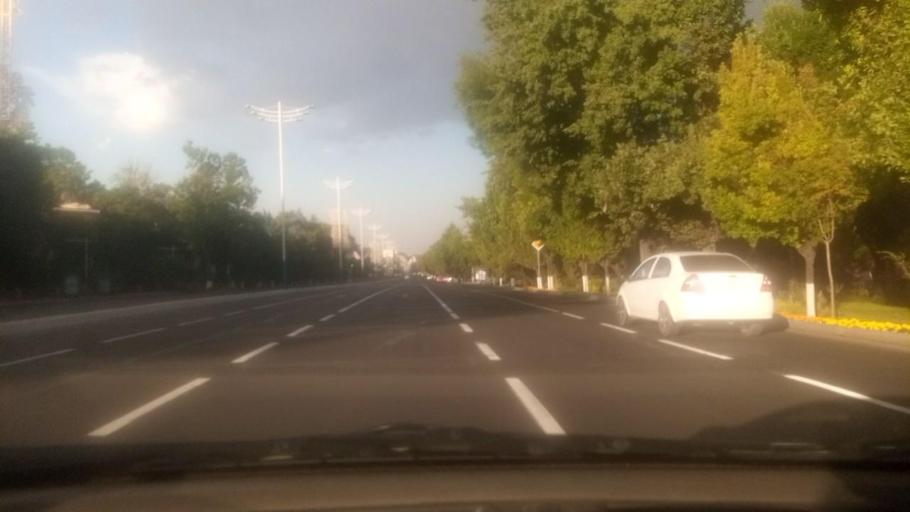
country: UZ
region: Toshkent
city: Salor
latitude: 41.3308
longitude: 69.3310
